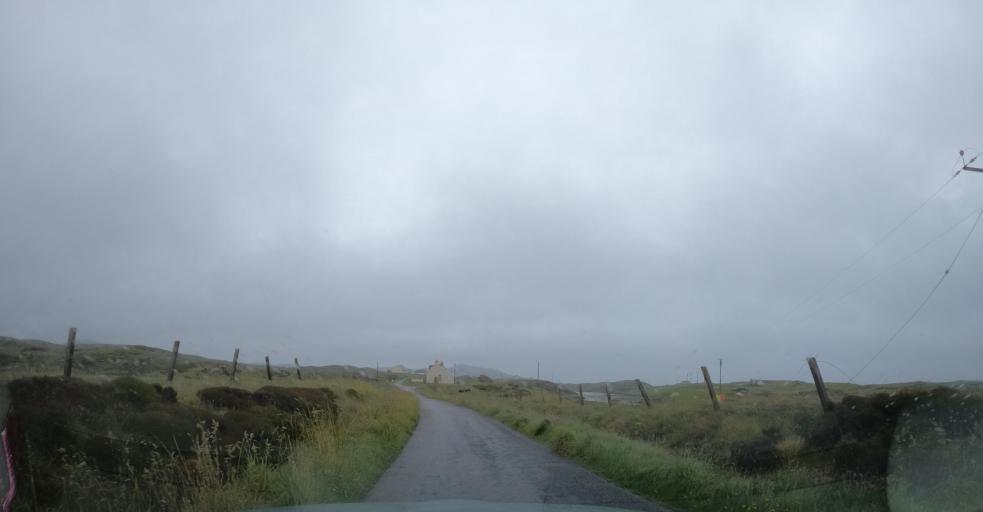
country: GB
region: Scotland
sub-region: Eilean Siar
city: Benbecula
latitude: 57.4787
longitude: -7.2204
